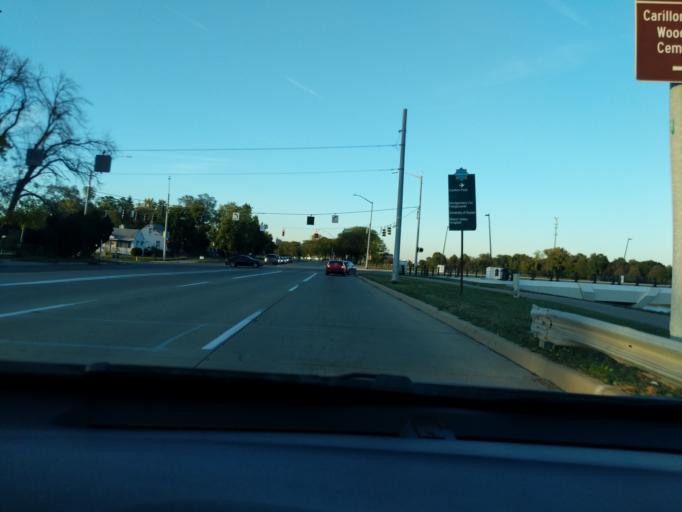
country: US
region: Ohio
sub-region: Montgomery County
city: Dayton
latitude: 39.7393
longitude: -84.1949
